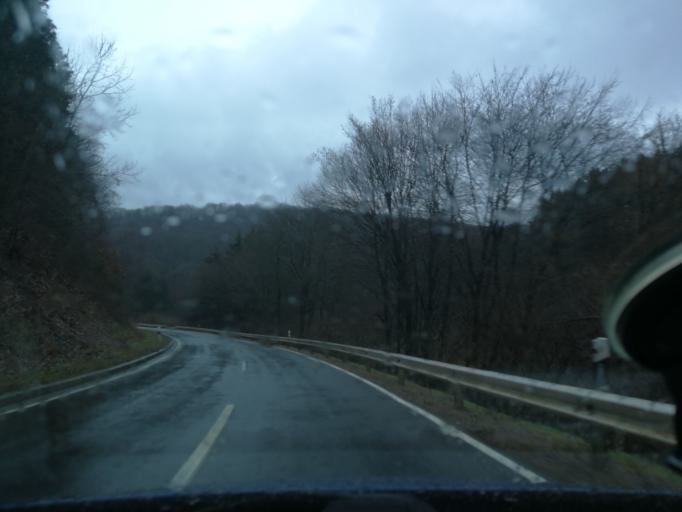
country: DE
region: Rheinland-Pfalz
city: Rorodt
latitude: 49.7598
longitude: 7.0626
